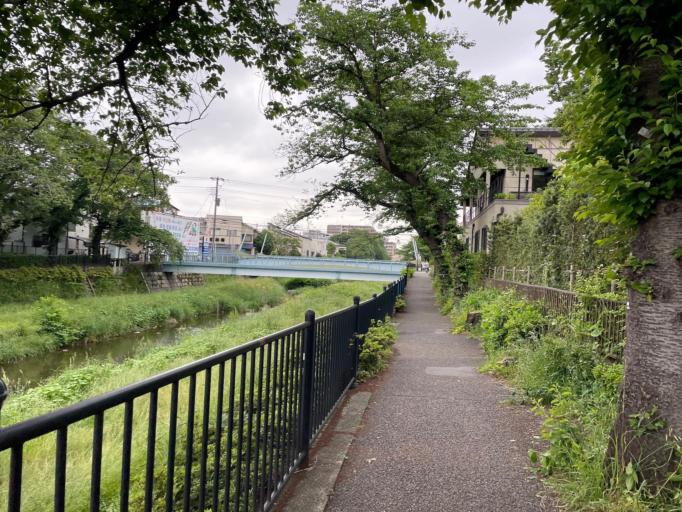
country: JP
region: Tokyo
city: Chofugaoka
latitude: 35.6589
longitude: 139.5530
